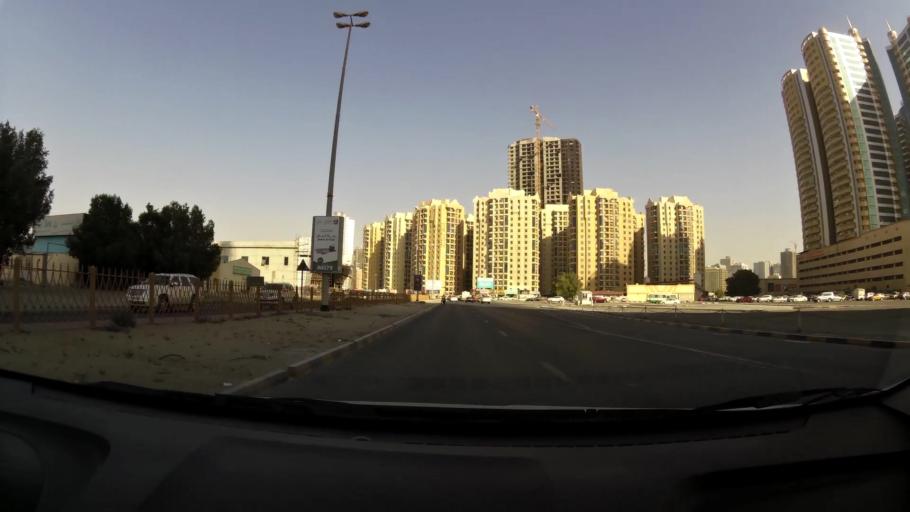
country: AE
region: Ajman
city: Ajman
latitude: 25.3965
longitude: 55.4552
